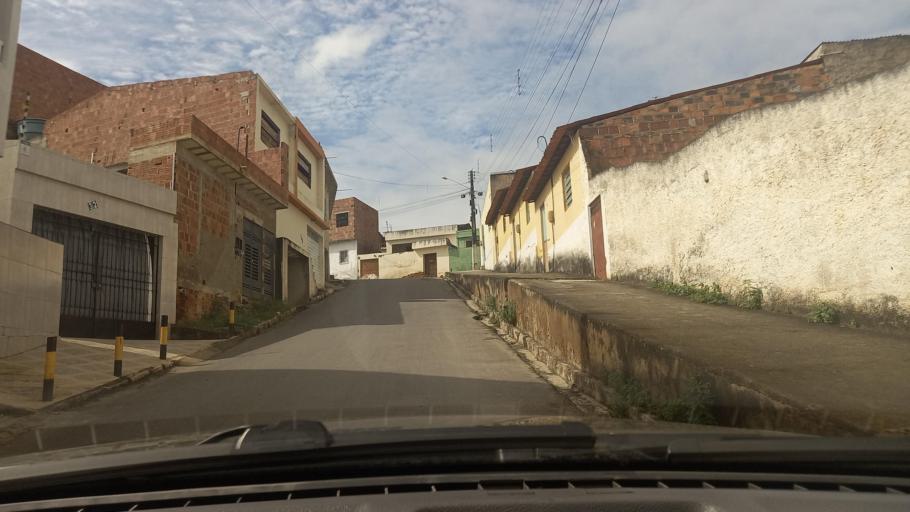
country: BR
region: Pernambuco
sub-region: Vitoria De Santo Antao
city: Vitoria de Santo Antao
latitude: -8.1226
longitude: -35.2894
